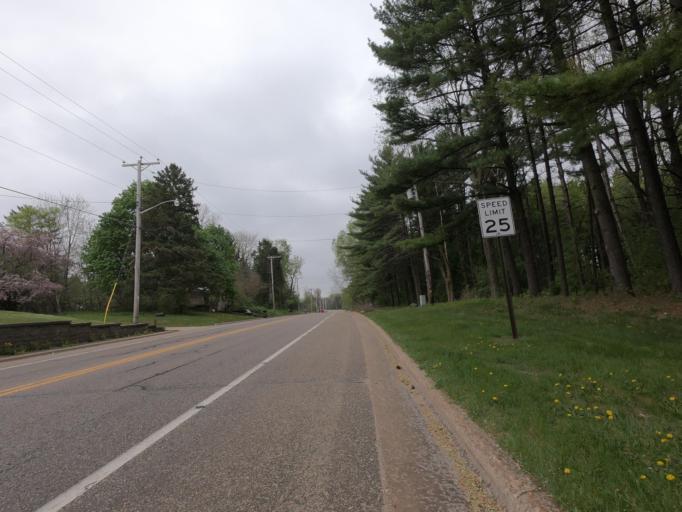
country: US
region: Wisconsin
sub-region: Jefferson County
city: Jefferson
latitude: 43.0208
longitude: -88.8105
